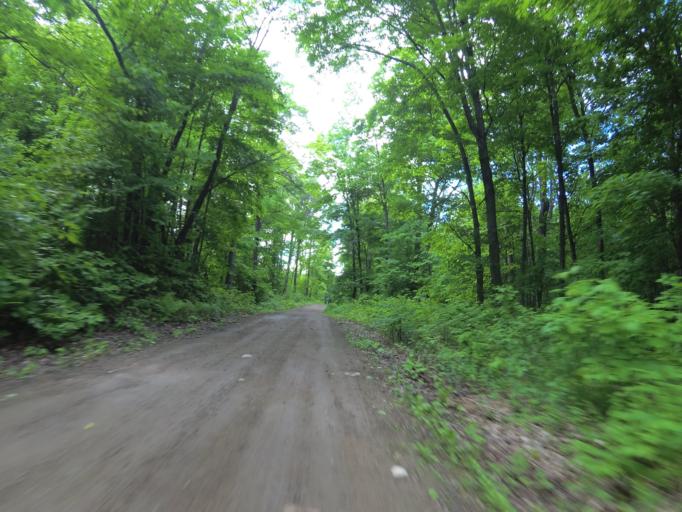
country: CA
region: Ontario
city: Renfrew
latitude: 45.1365
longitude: -76.8763
